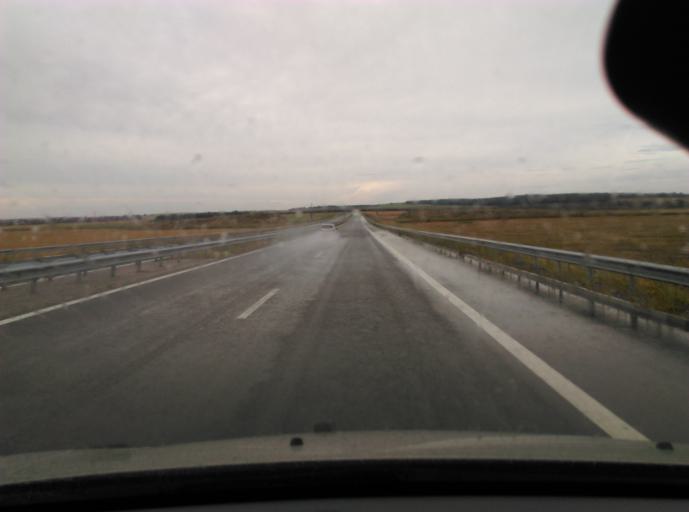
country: BG
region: Khaskovo
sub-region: Obshtina Dimitrovgrad
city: Dimitrovgrad
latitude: 42.0320
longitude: 25.5492
